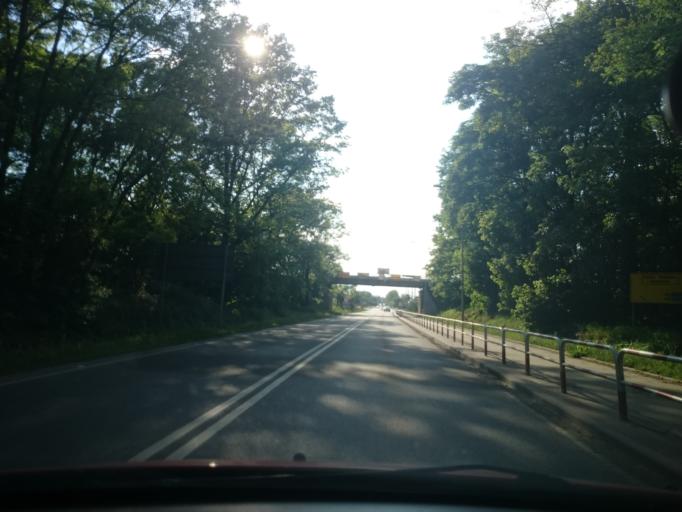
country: PL
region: Opole Voivodeship
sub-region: Powiat strzelecki
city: Strzelce Opolskie
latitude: 50.5030
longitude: 18.3333
